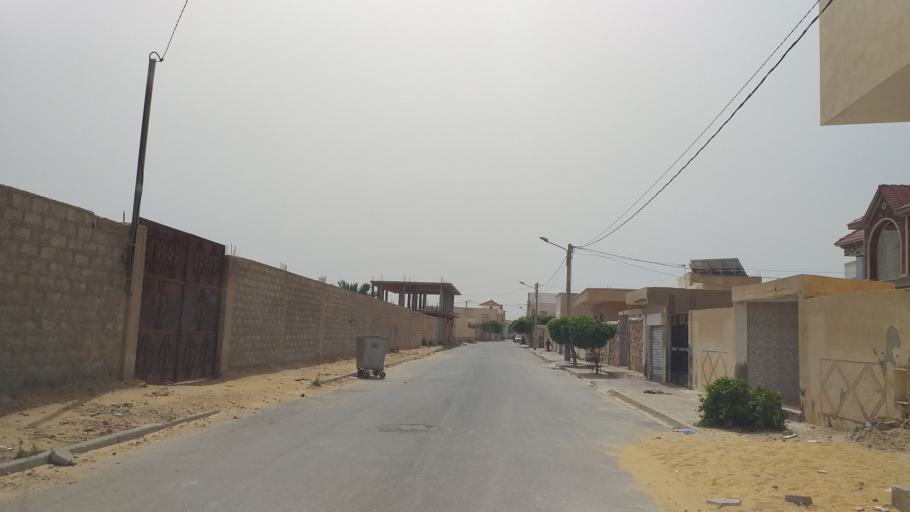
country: TN
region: Qabis
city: Gabes
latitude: 33.9432
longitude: 10.0574
